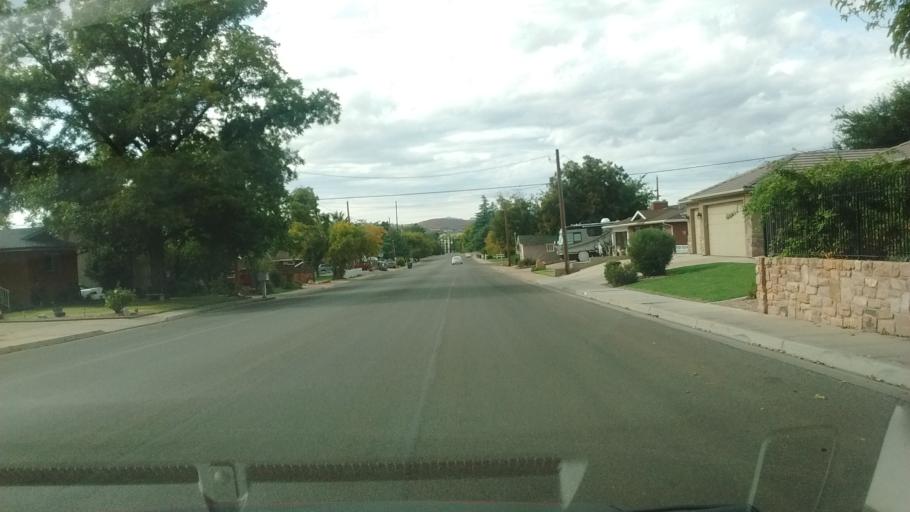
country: US
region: Utah
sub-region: Washington County
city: Washington
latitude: 37.1339
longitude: -113.5068
